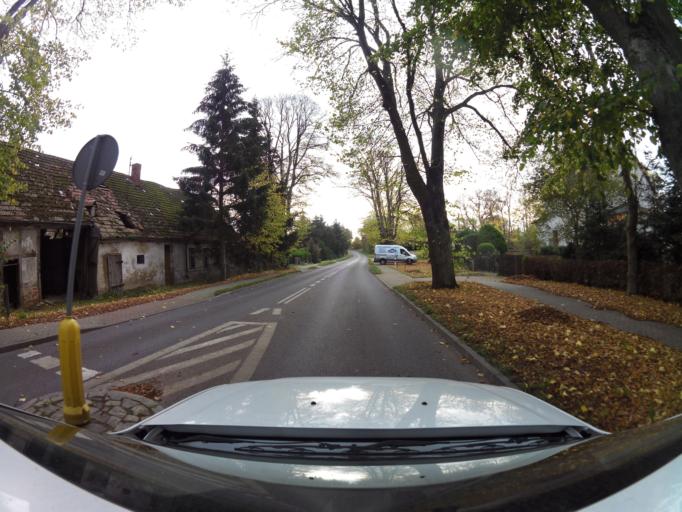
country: PL
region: West Pomeranian Voivodeship
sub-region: Powiat gryficki
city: Karnice
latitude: 54.0688
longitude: 15.0746
